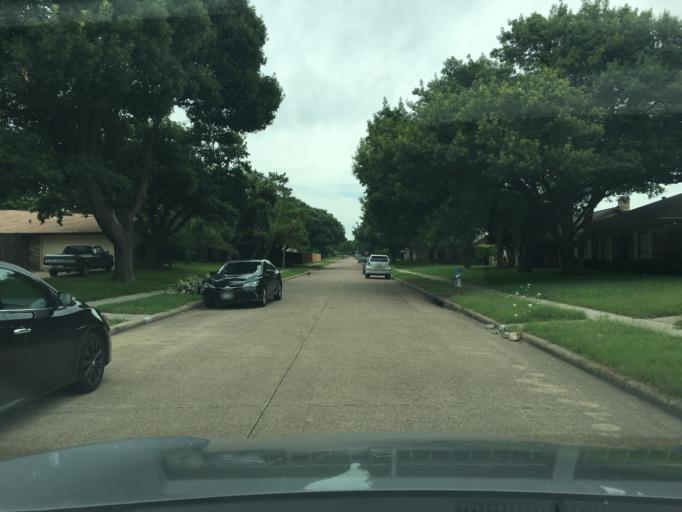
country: US
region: Texas
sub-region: Dallas County
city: Richardson
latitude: 32.9342
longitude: -96.7100
